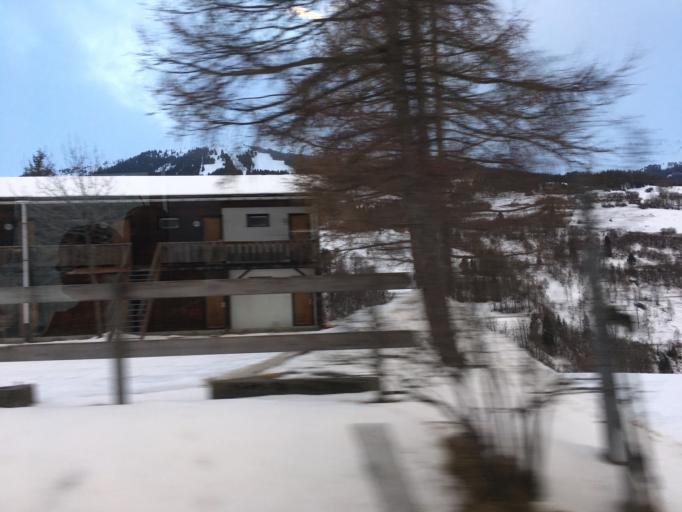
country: CH
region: Grisons
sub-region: Albula District
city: Tiefencastel
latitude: 46.6013
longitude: 9.5934
